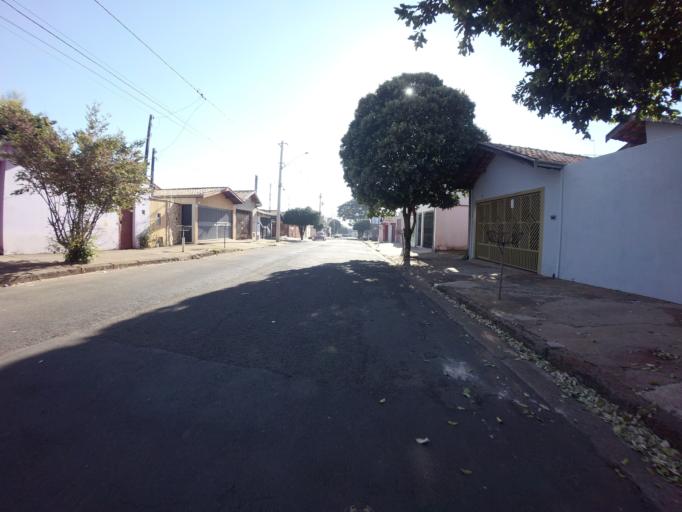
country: BR
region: Sao Paulo
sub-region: Piracicaba
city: Piracicaba
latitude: -22.7681
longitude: -47.5895
